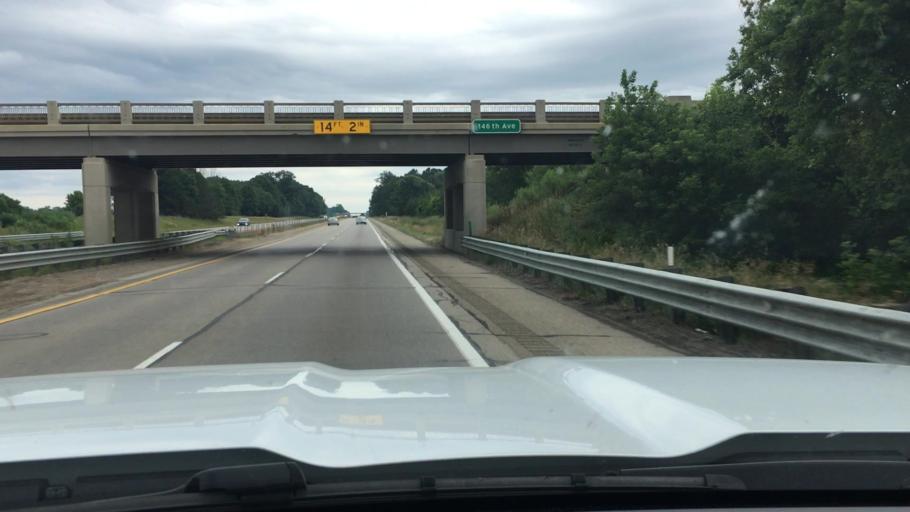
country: US
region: Michigan
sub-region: Kent County
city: Byron Center
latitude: 42.7542
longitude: -85.6737
